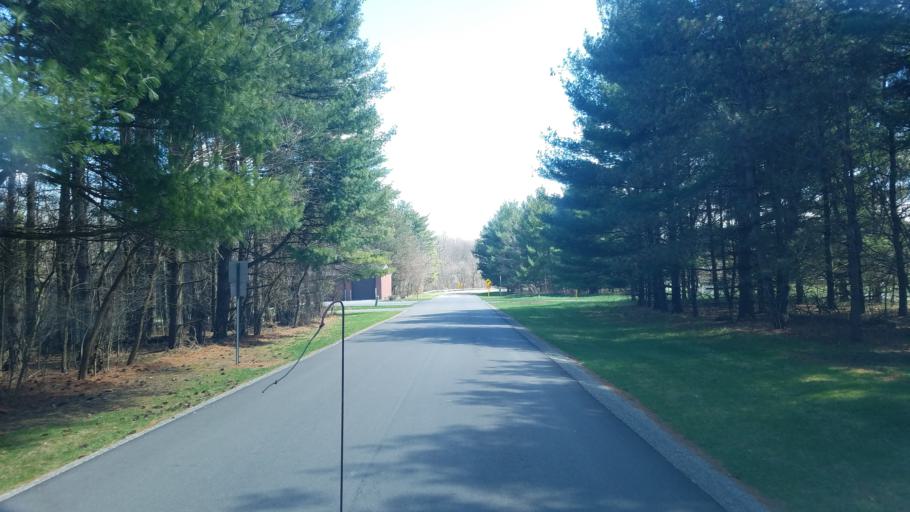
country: US
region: Ohio
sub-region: Hancock County
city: Findlay
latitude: 41.0338
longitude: -83.5633
